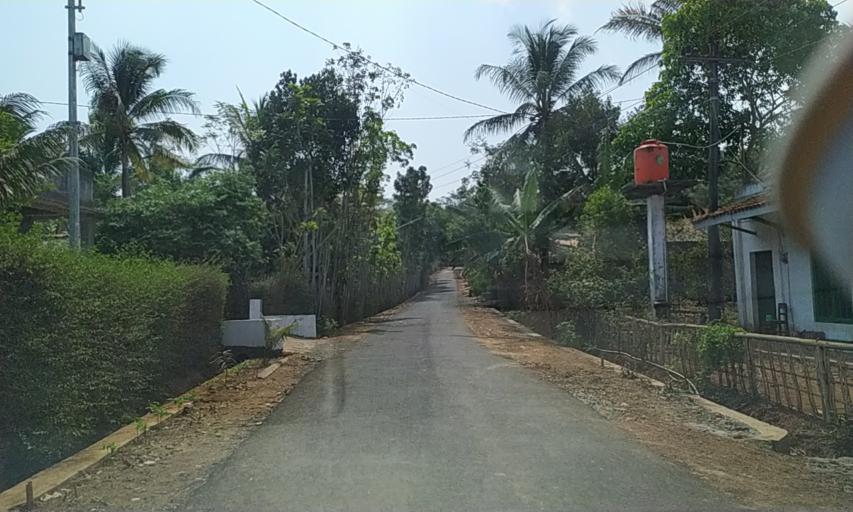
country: ID
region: Central Java
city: Rungkang
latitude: -7.4335
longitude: 108.8488
